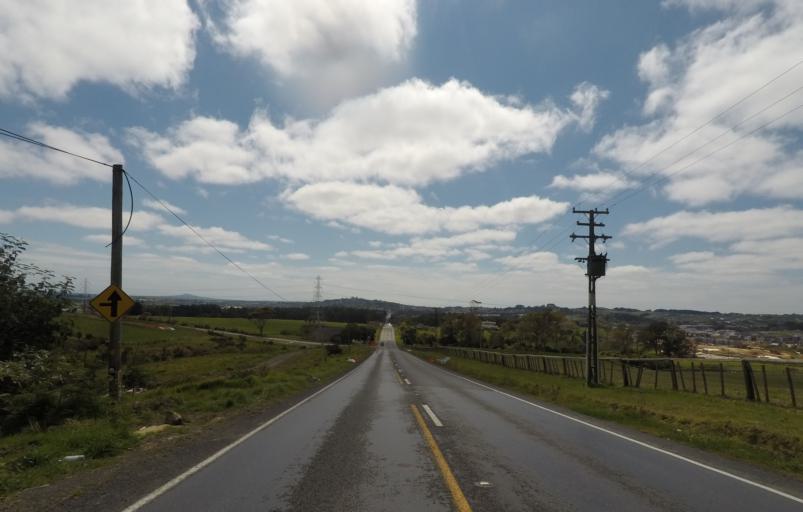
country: NZ
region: Auckland
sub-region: Auckland
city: Manukau City
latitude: -36.9880
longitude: 174.9188
